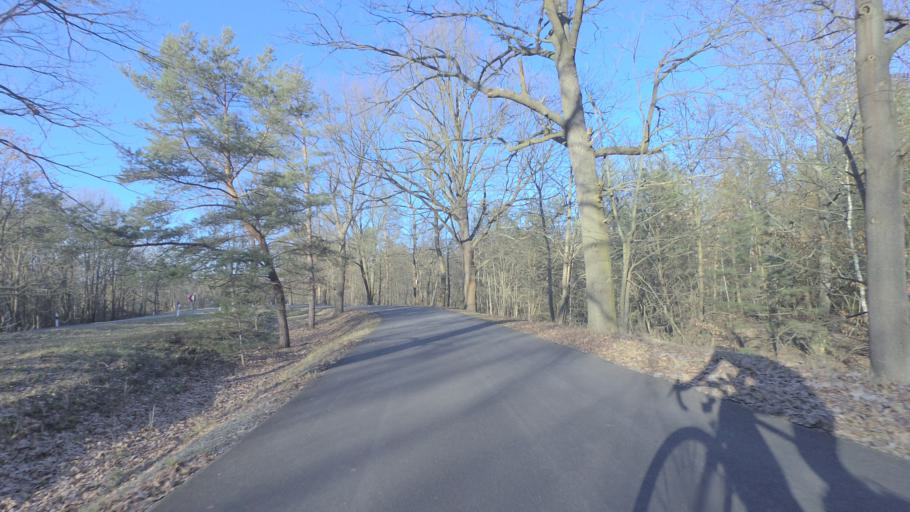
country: DE
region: Brandenburg
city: Sperenberg
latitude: 52.0225
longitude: 13.3190
